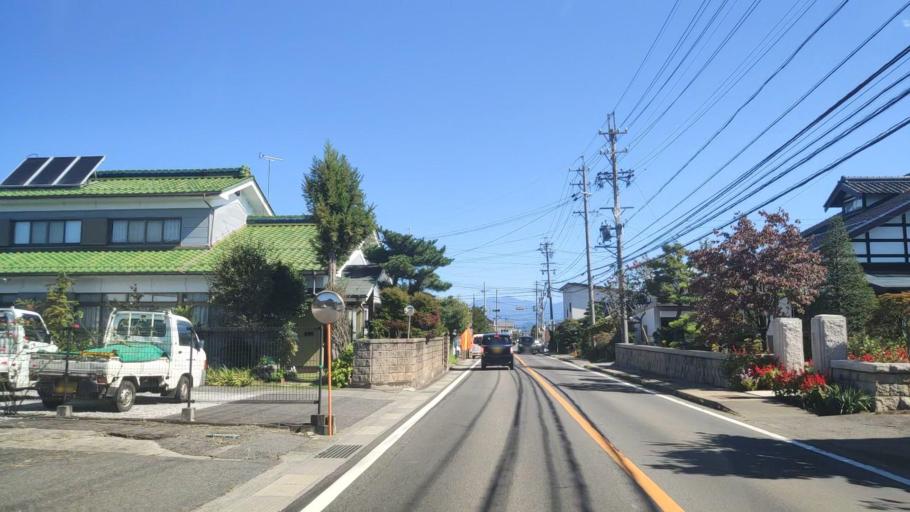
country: JP
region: Nagano
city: Shiojiri
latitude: 36.1437
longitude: 137.9423
